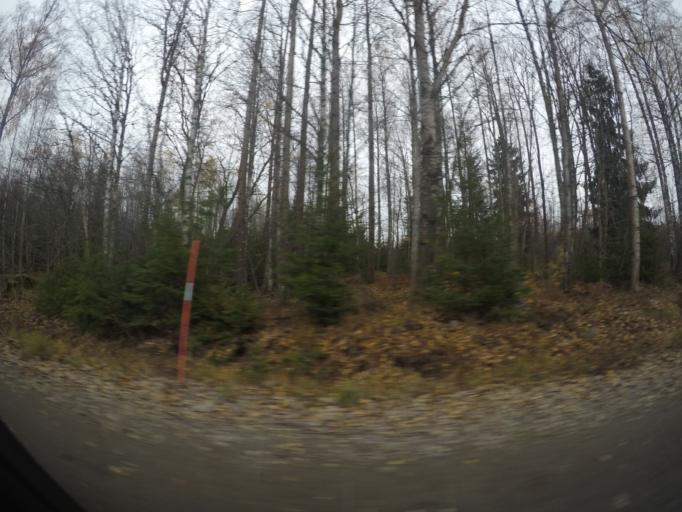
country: SE
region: Vaestmanland
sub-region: Surahammars Kommun
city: Ramnas
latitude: 59.7186
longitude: 16.0928
